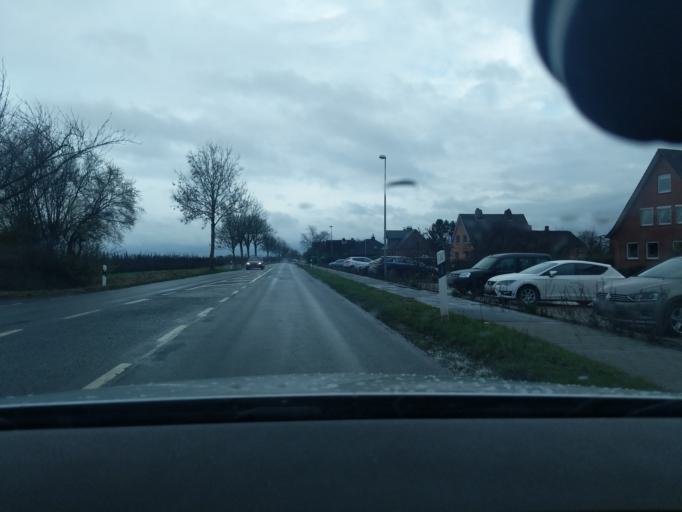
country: DE
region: Lower Saxony
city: Jork
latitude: 53.5598
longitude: 9.6560
